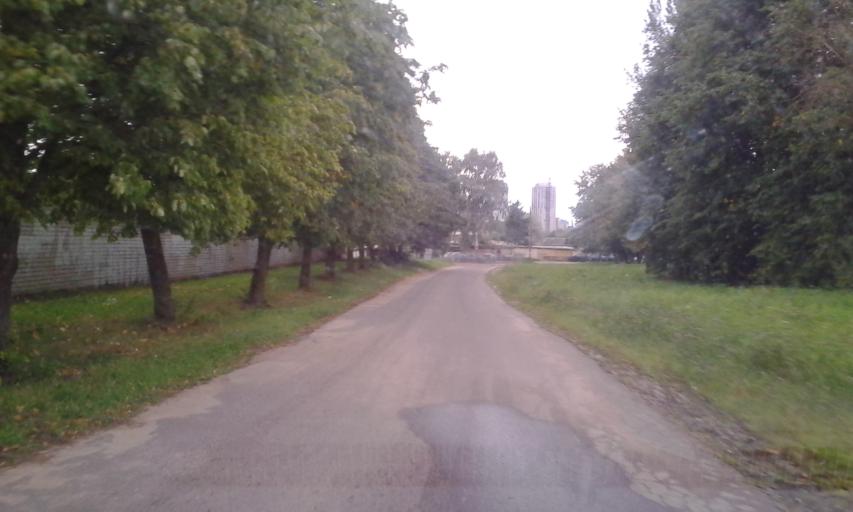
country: BY
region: Minsk
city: Minsk
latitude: 53.9462
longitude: 27.5703
